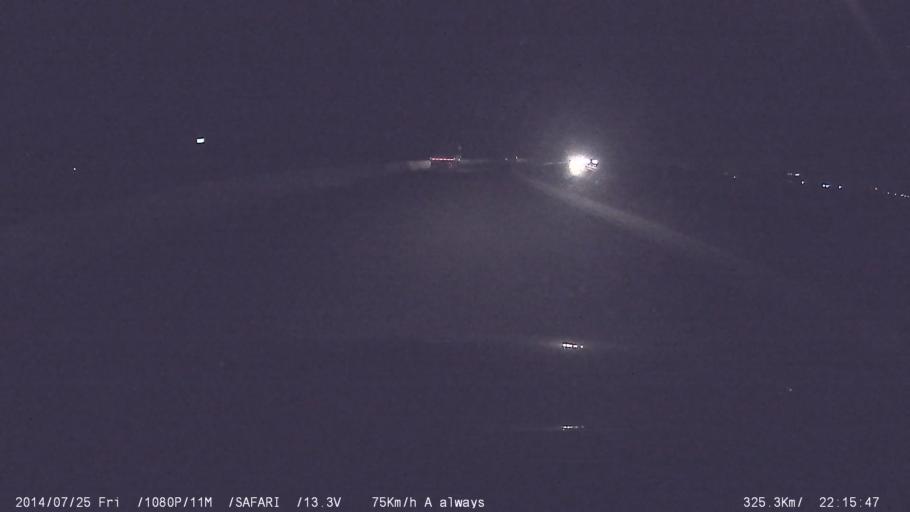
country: IN
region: Tamil Nadu
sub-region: Tiruppur
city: Avinashi
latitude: 11.1294
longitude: 77.1983
